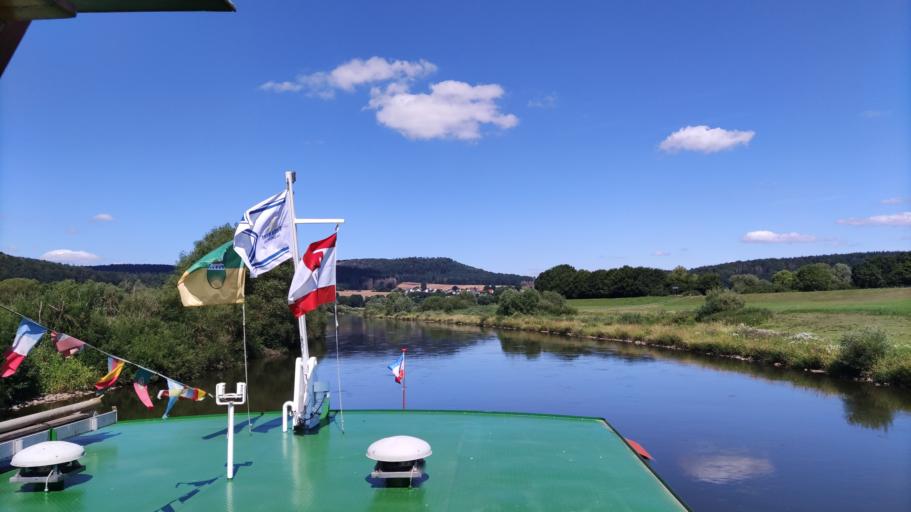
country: DE
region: North Rhine-Westphalia
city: Beverungen
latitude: 51.6815
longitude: 9.3950
